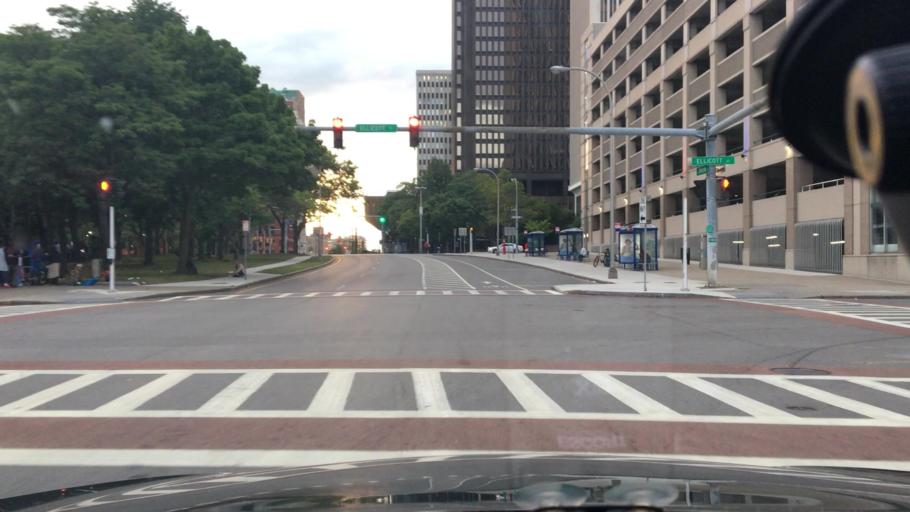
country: US
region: New York
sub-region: Erie County
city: Buffalo
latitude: 42.8830
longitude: -78.8727
